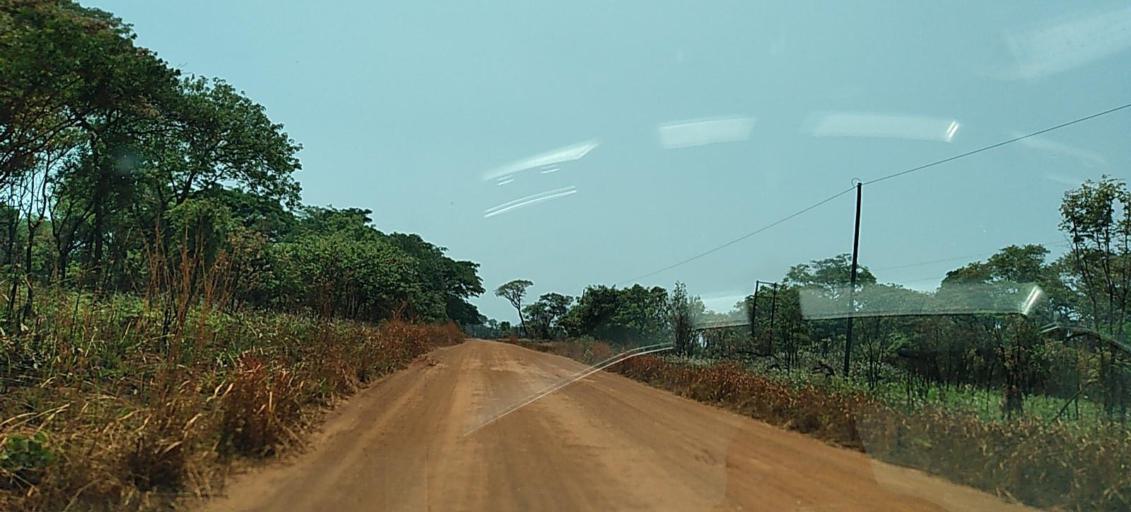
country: CD
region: Katanga
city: Kipushi
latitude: -11.9862
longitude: 26.8736
